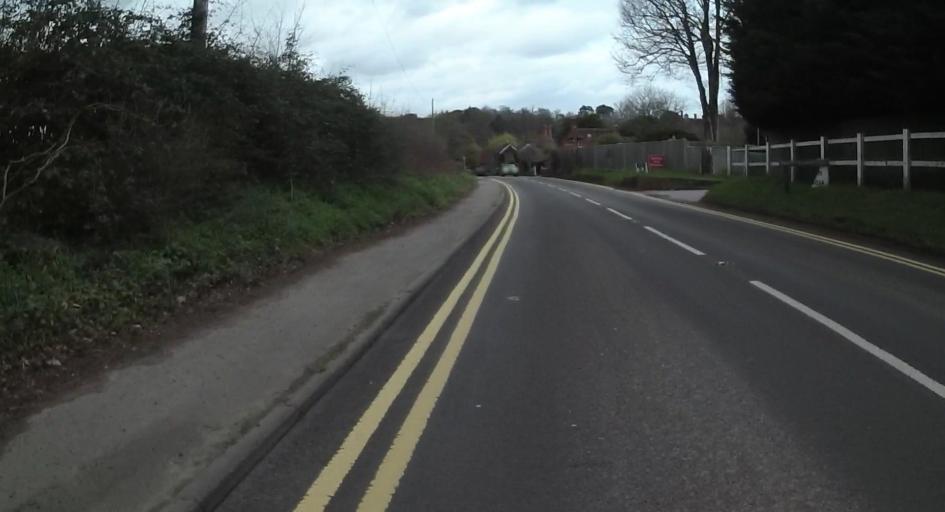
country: GB
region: England
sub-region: Surrey
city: Churt
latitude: 51.1686
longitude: -0.7870
